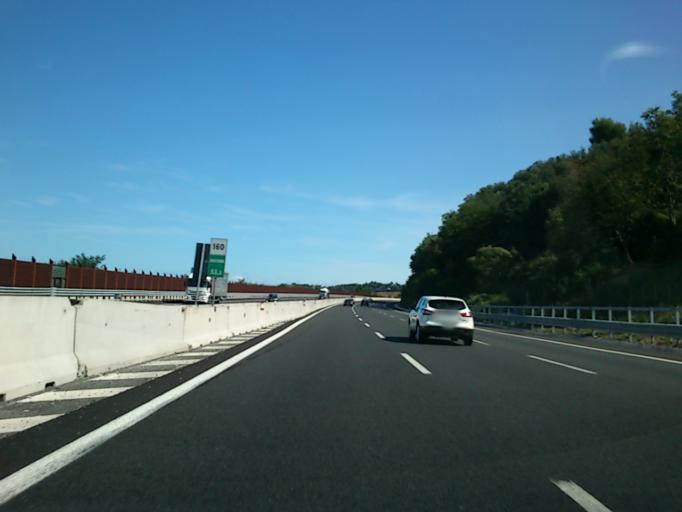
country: IT
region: The Marches
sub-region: Provincia di Pesaro e Urbino
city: Pesaro
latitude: 43.8888
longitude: 12.8918
